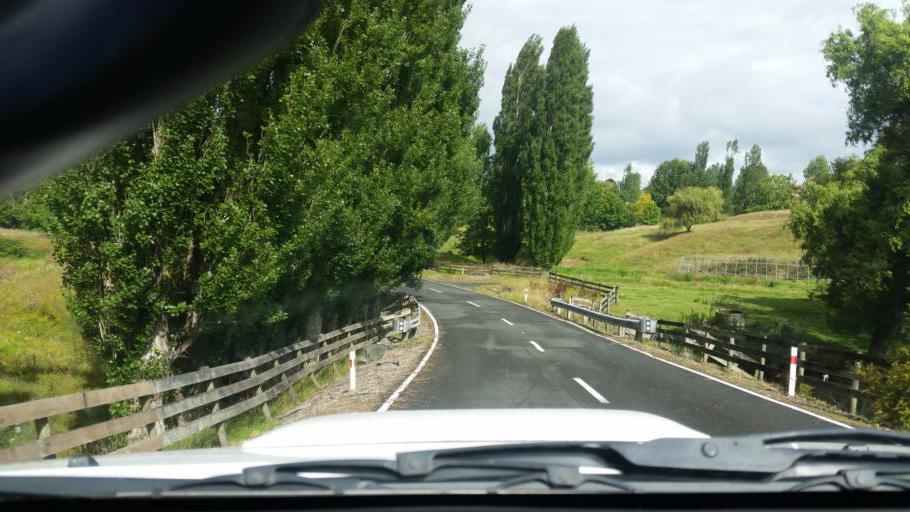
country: NZ
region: Auckland
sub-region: Auckland
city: Wellsford
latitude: -36.1313
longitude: 174.3617
